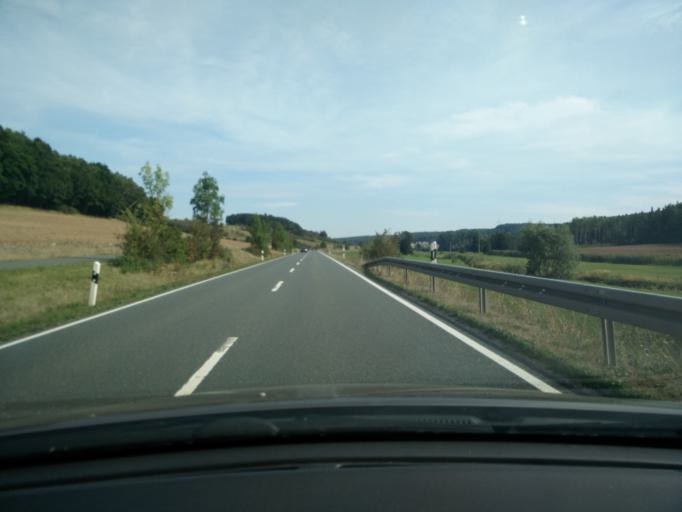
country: DE
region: Bavaria
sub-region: Regierungsbezirk Mittelfranken
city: Wilhelmsdorf
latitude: 49.5583
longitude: 10.7552
